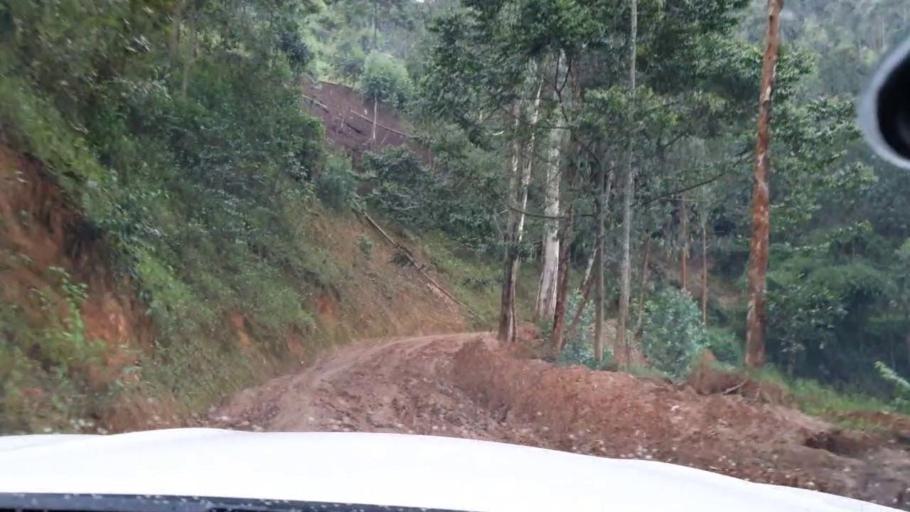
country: RW
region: Western Province
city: Cyangugu
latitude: -2.4116
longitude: 29.1881
